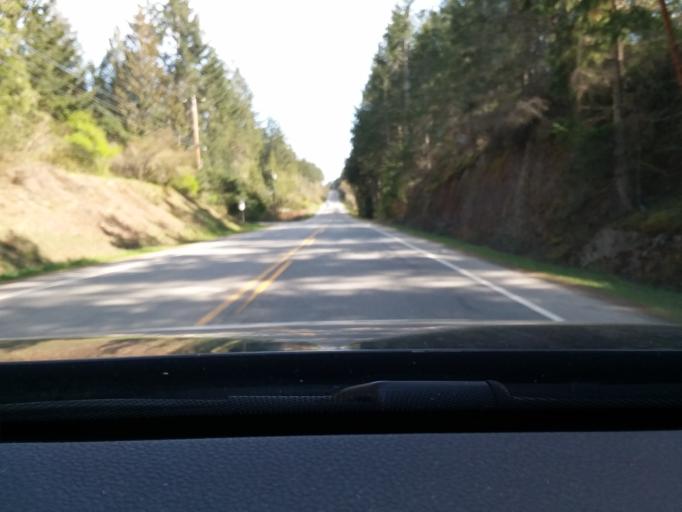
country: CA
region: British Columbia
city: North Cowichan
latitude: 48.8628
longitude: -123.4927
